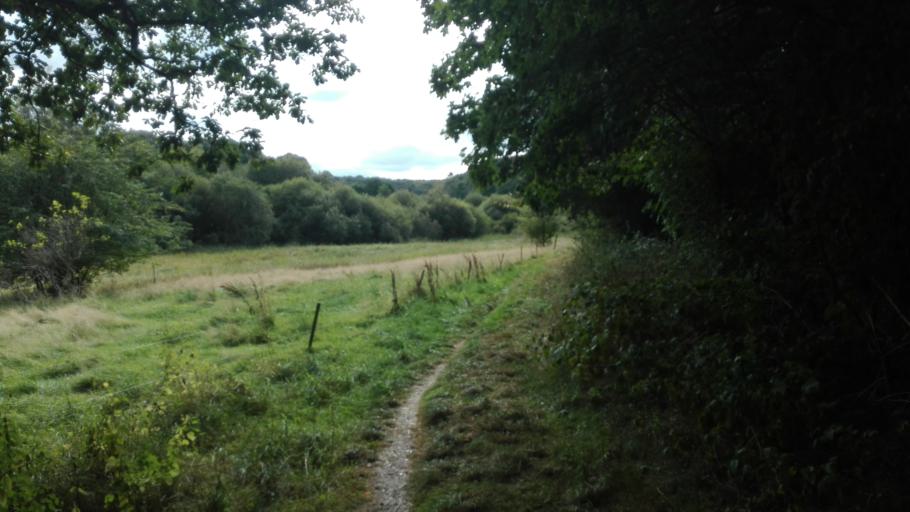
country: DK
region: Central Jutland
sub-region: Skanderborg Kommune
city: Stilling
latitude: 56.0957
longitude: 9.9815
